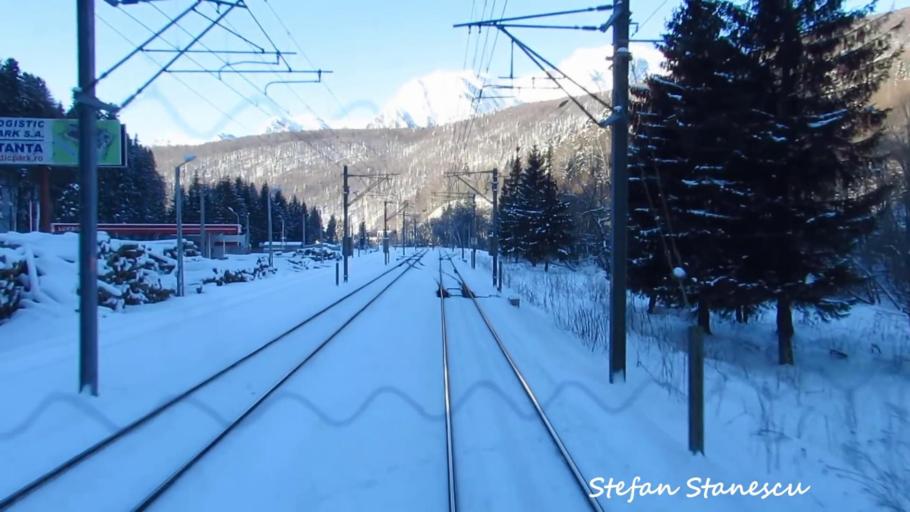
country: RO
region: Prahova
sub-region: Oras Azuga
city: Azuga
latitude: 45.4510
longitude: 25.5603
